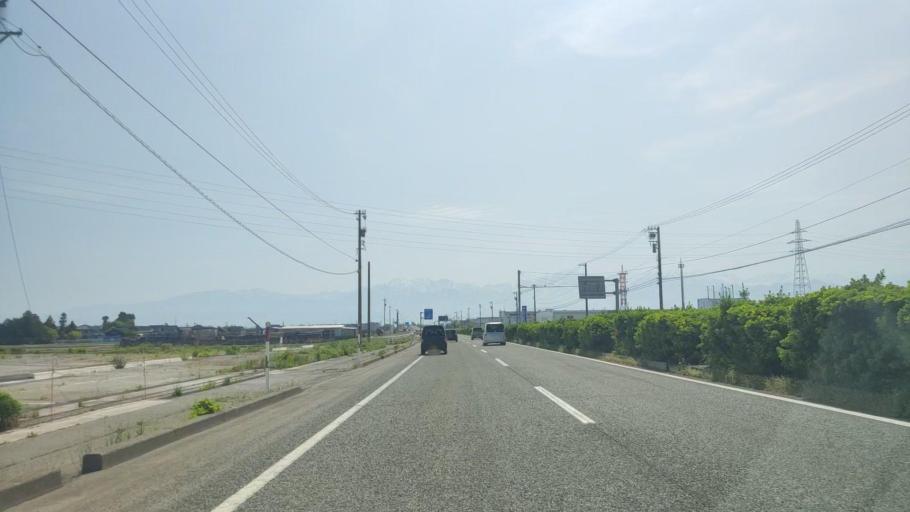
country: JP
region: Toyama
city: Toyama-shi
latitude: 36.7210
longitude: 137.2534
